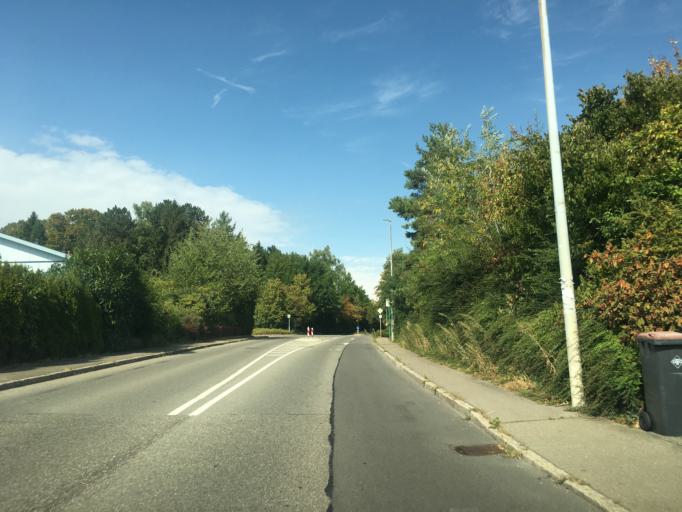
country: DE
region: Baden-Wuerttemberg
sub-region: Tuebingen Region
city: Gomaringen
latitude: 48.4396
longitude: 9.1481
